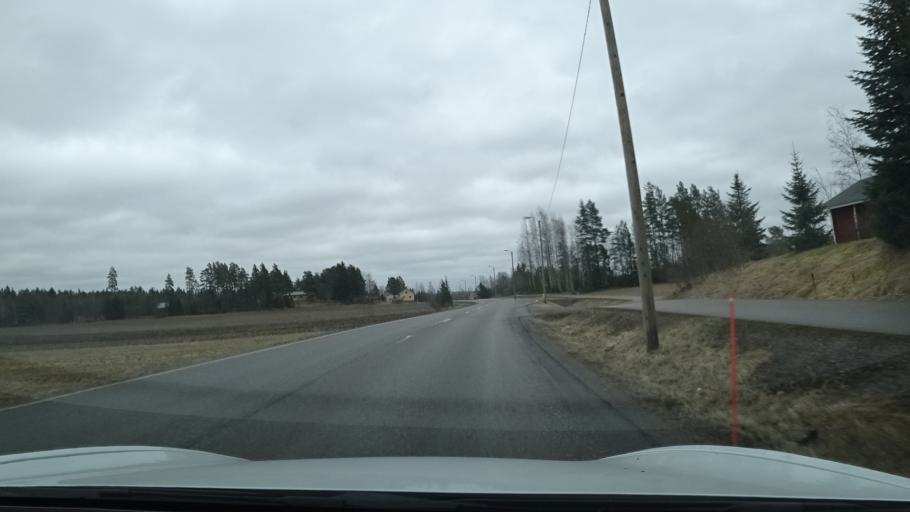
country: FI
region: Uusimaa
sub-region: Porvoo
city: Askola
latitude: 60.4959
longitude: 25.5054
